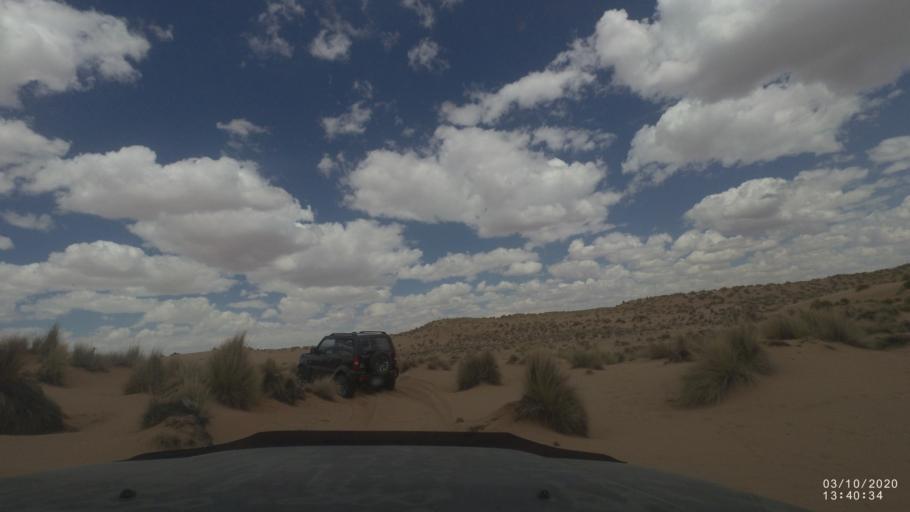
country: BO
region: Oruro
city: Poopo
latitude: -18.6915
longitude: -67.5314
